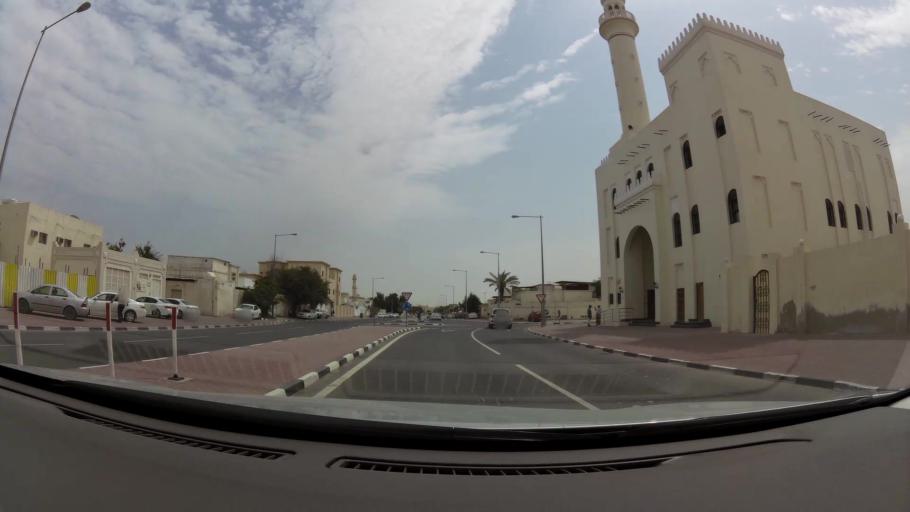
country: QA
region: Baladiyat ar Rayyan
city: Ar Rayyan
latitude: 25.3289
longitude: 51.4713
